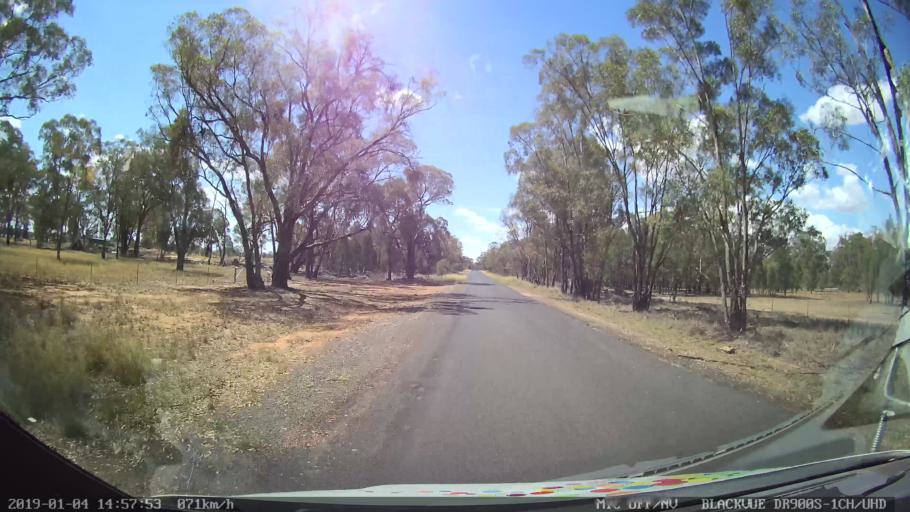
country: AU
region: New South Wales
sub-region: Gilgandra
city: Gilgandra
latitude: -31.9616
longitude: 148.6309
